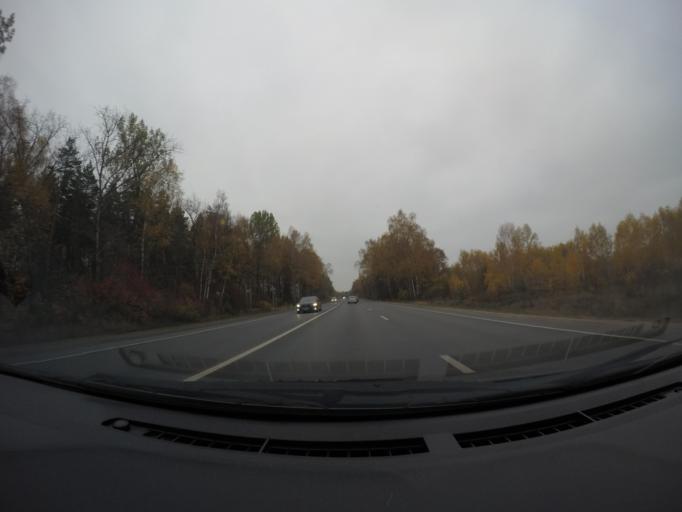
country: RU
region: Moskovskaya
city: Malyshevo
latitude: 55.4561
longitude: 38.3277
